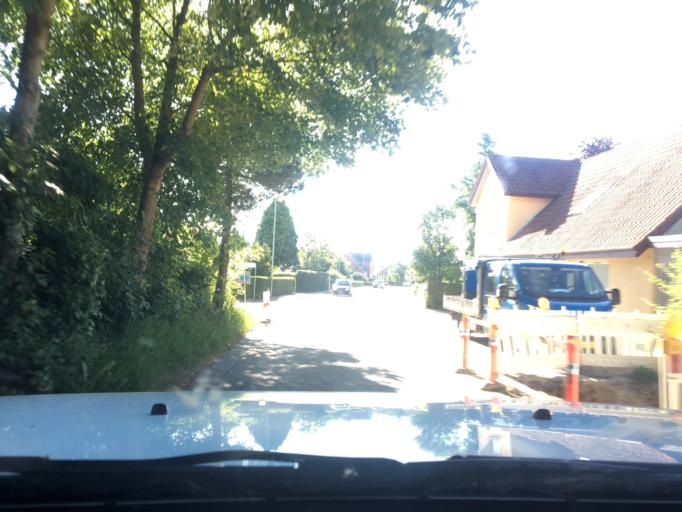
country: DK
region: Central Jutland
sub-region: Syddjurs Kommune
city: Hornslet
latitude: 56.3213
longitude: 10.3062
